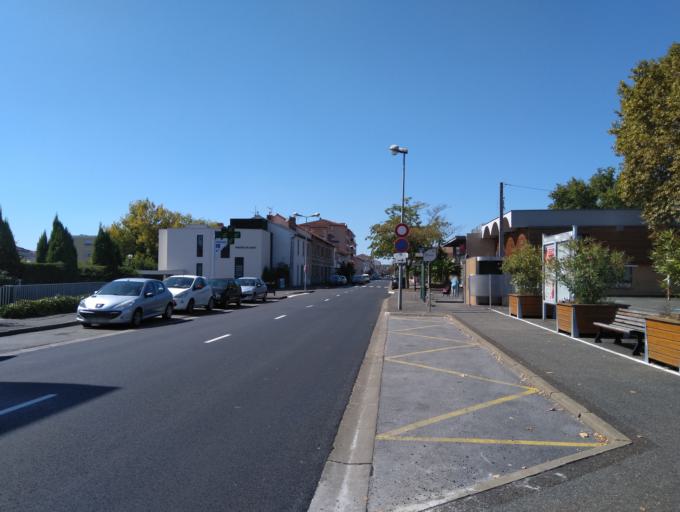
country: FR
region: Aquitaine
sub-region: Departement des Landes
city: Dax
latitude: 43.7064
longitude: -1.0404
